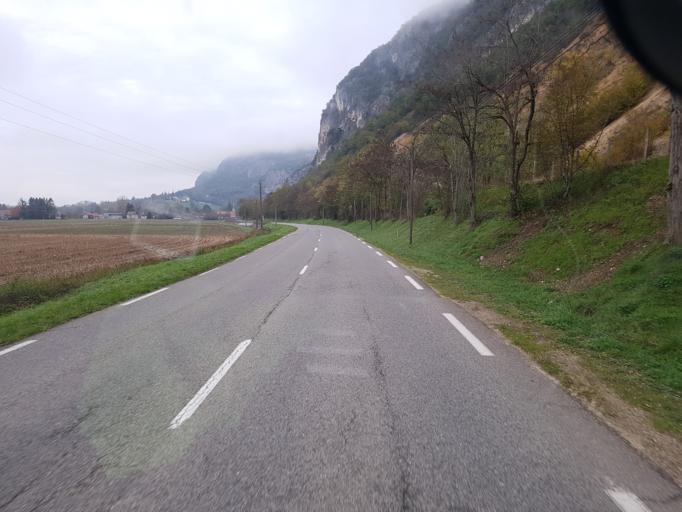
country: FR
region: Rhone-Alpes
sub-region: Departement de la Savoie
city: Yenne
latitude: 45.6968
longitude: 5.7173
